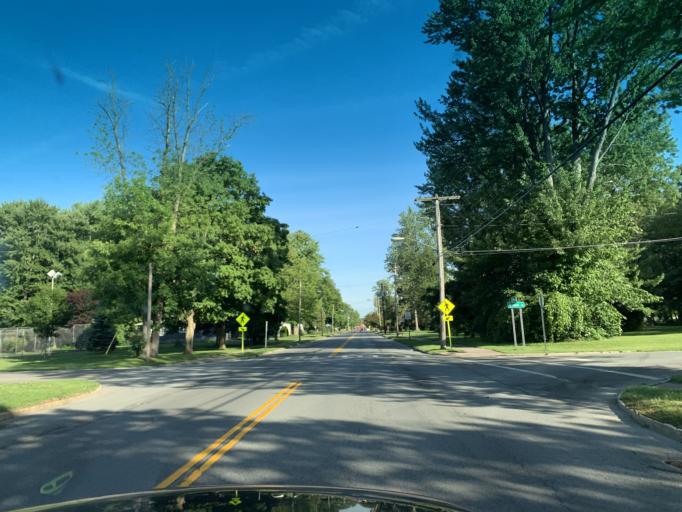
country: US
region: New York
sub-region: Madison County
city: Oneida
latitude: 43.1019
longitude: -75.6584
